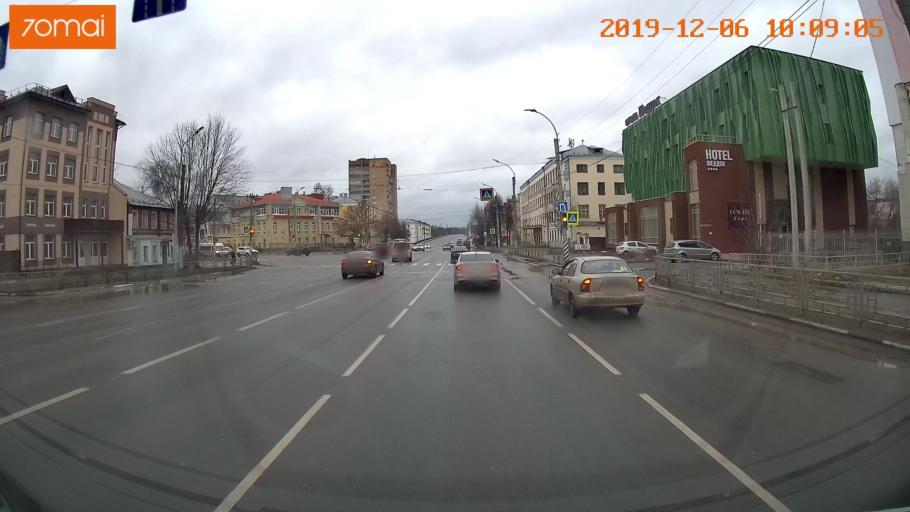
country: RU
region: Ivanovo
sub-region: Gorod Ivanovo
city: Ivanovo
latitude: 57.0205
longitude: 40.9684
